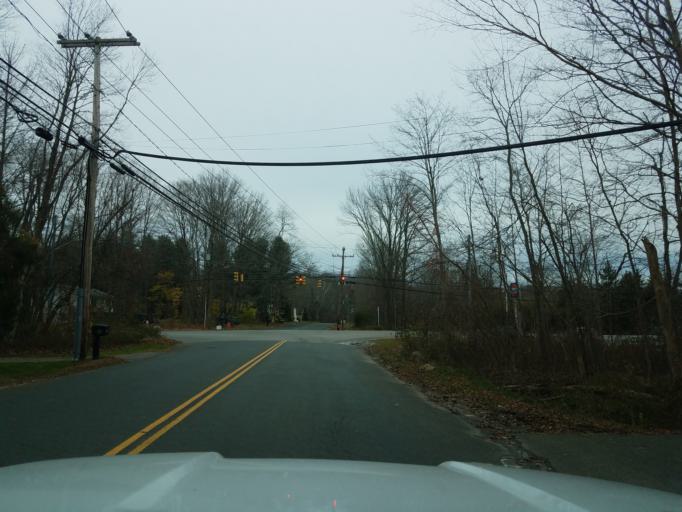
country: US
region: Connecticut
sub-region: New Haven County
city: North Branford
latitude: 41.3497
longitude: -72.7283
